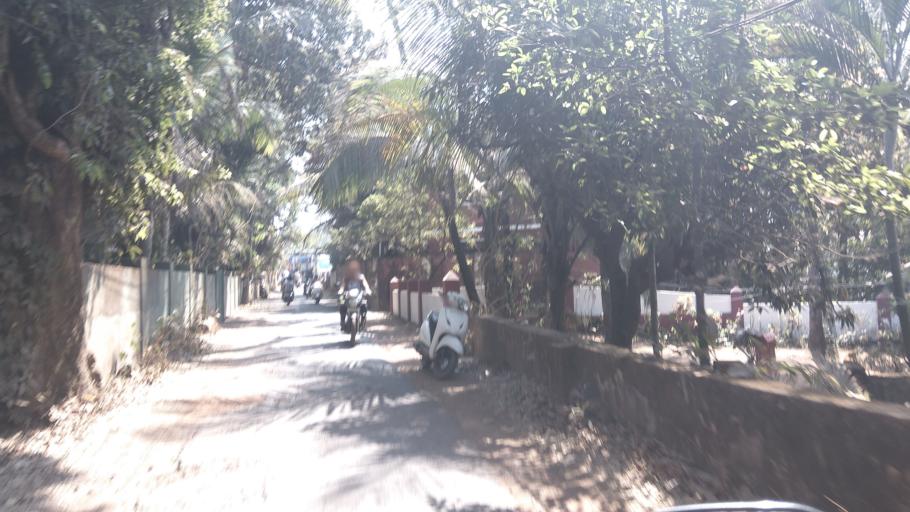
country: IN
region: Goa
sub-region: North Goa
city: Vagator
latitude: 15.6003
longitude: 73.7398
